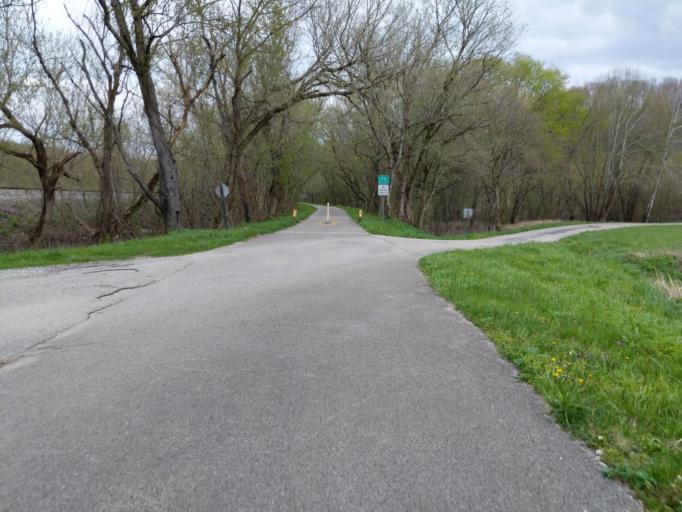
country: US
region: Ohio
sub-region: Athens County
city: Chauncey
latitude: 39.3883
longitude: -82.1260
